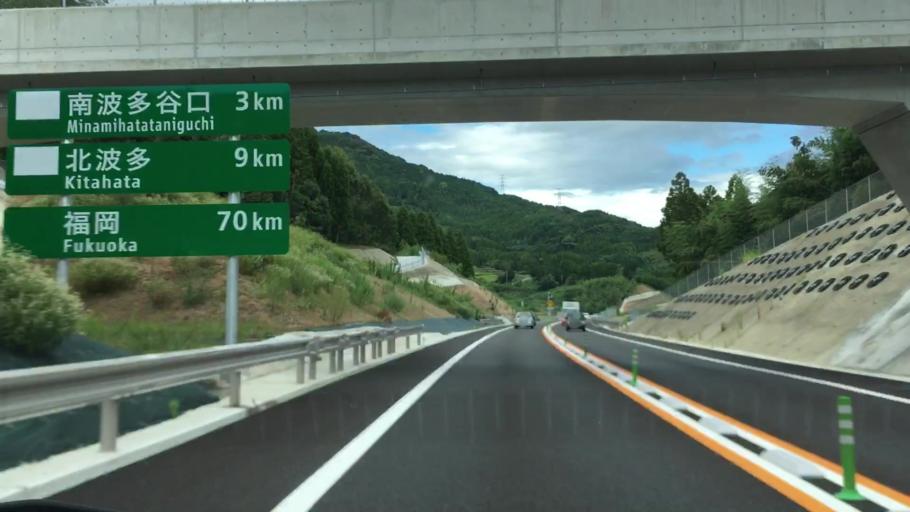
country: JP
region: Saga Prefecture
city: Imaricho-ko
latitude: 33.3089
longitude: 129.9165
